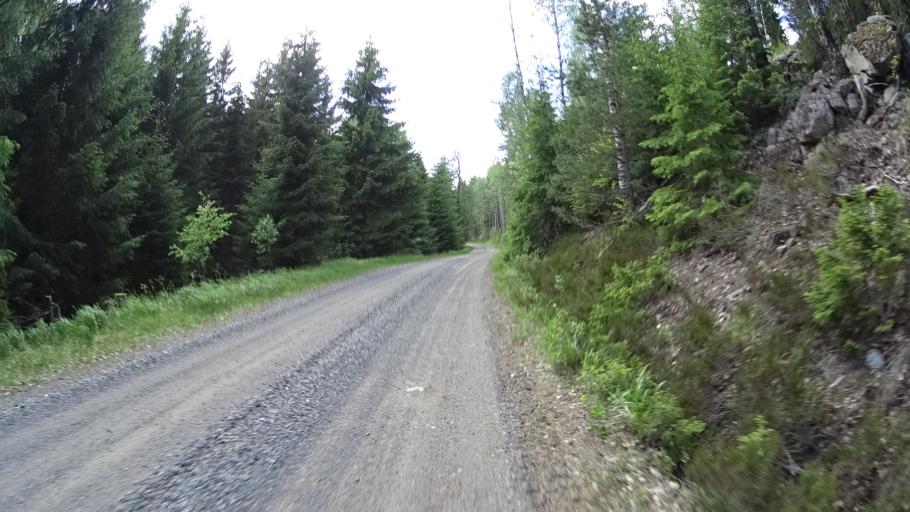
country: FI
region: Varsinais-Suomi
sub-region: Salo
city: Kisko
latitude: 60.1791
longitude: 23.5164
